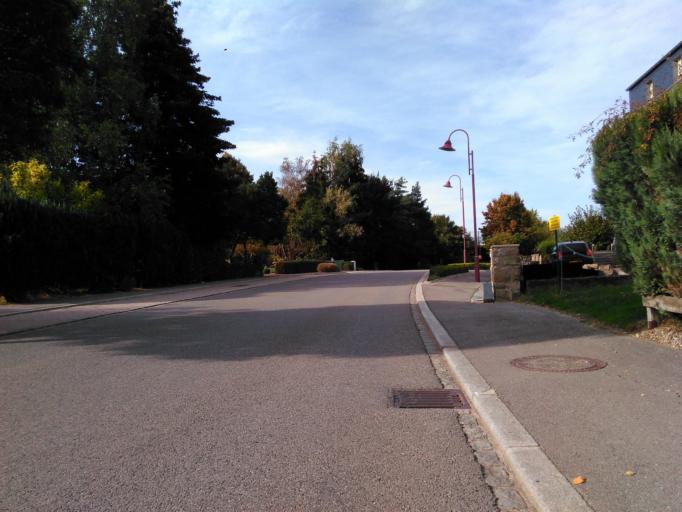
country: LU
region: Luxembourg
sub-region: Canton de Capellen
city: Steinfort
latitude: 49.6361
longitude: 5.9146
